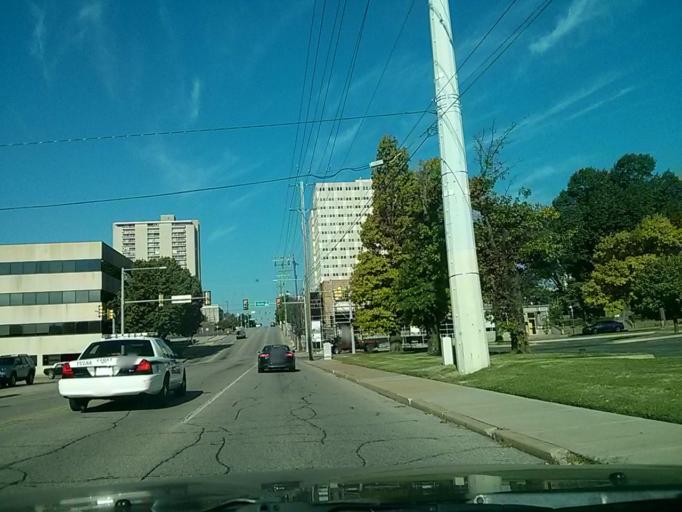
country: US
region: Oklahoma
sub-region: Tulsa County
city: Tulsa
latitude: 36.1407
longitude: -95.9844
